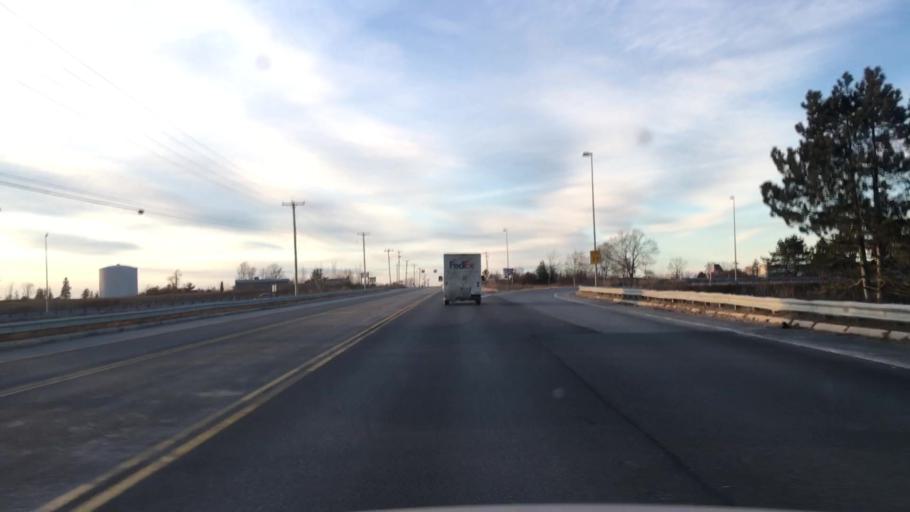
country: US
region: Maine
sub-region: Penobscot County
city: Holden
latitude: 44.7715
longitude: -68.7218
